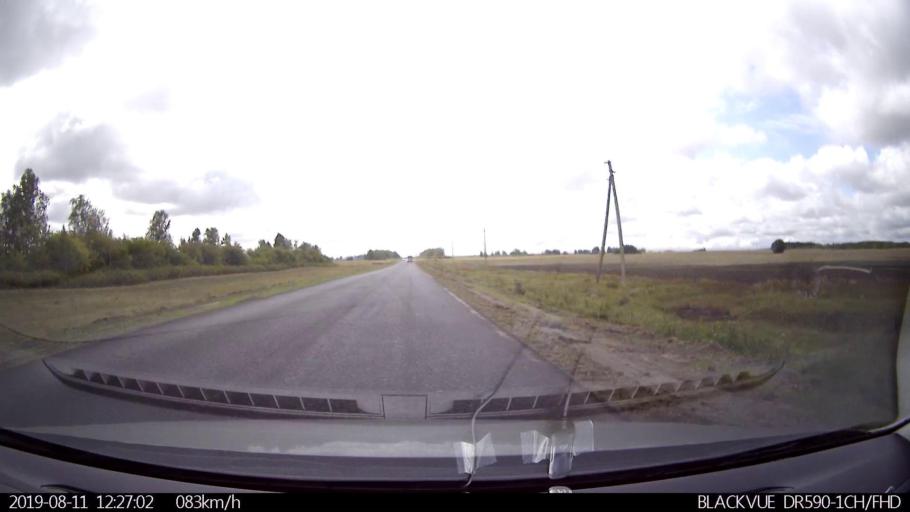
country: RU
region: Ulyanovsk
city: Ignatovka
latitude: 53.8585
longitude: 47.9254
